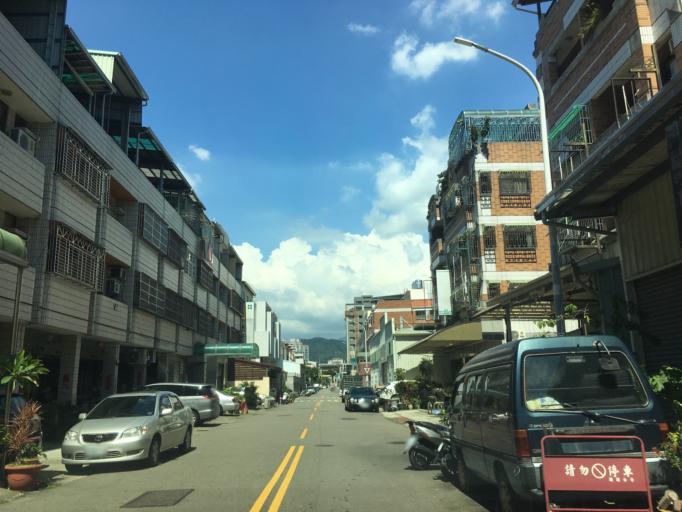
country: TW
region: Taiwan
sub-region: Taichung City
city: Taichung
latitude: 24.1450
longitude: 120.7068
